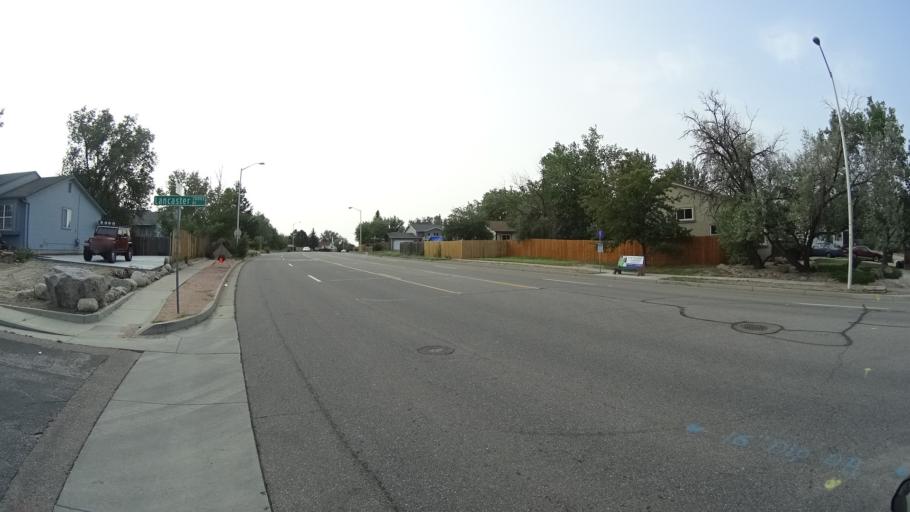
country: US
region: Colorado
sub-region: El Paso County
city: Stratmoor
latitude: 38.8041
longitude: -104.7449
